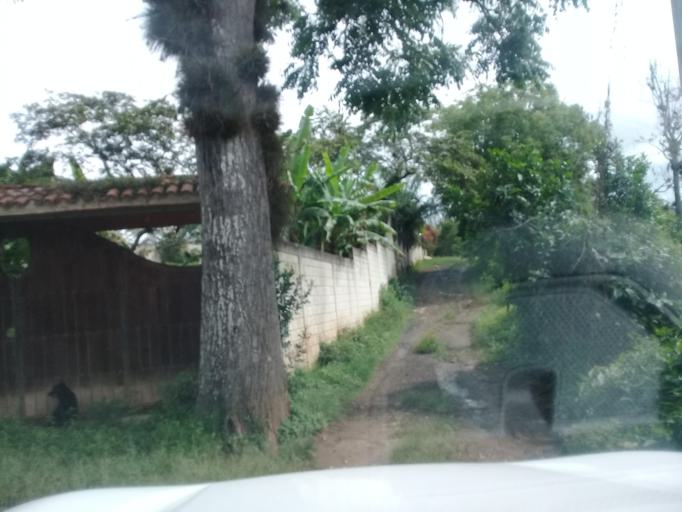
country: MX
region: Veracruz
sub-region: Emiliano Zapata
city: Jacarandas
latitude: 19.4823
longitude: -96.8532
